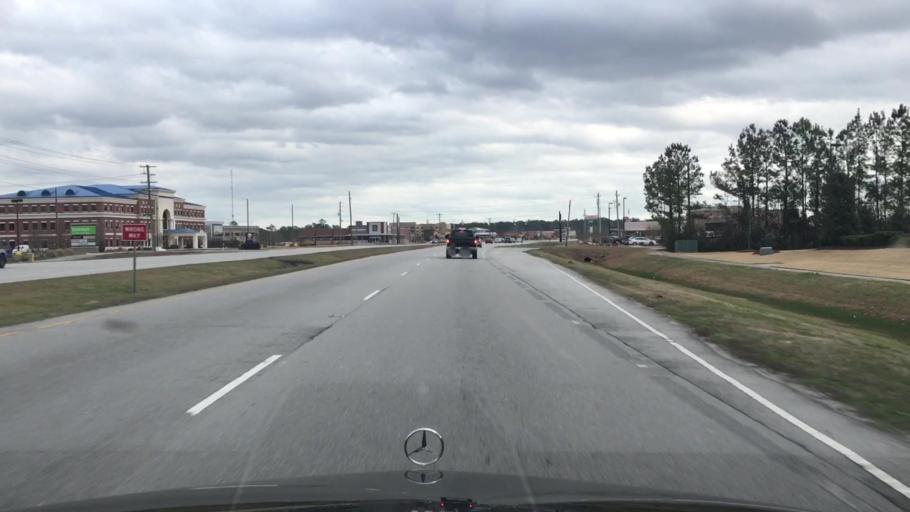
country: US
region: North Carolina
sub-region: Onslow County
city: Pumpkin Center
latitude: 34.7998
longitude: -77.4170
